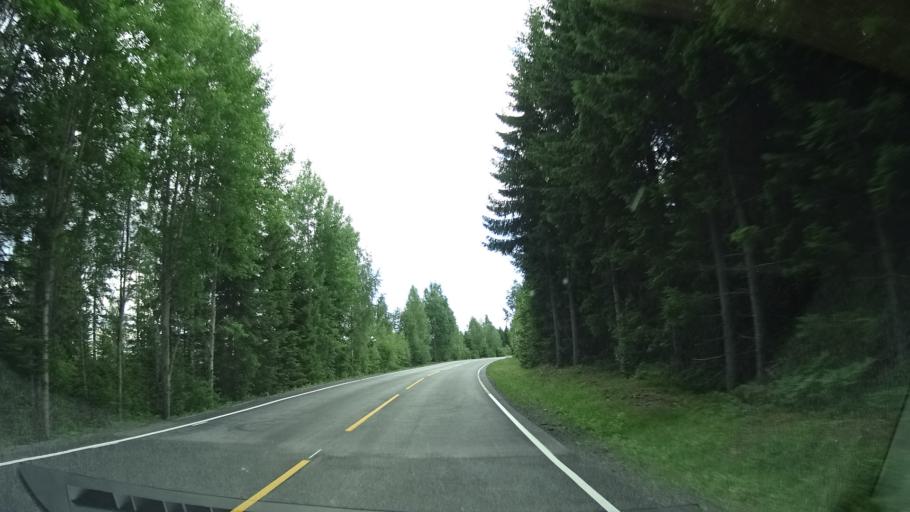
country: NO
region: Ostfold
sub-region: Marker
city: Orje
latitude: 59.5039
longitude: 11.6340
